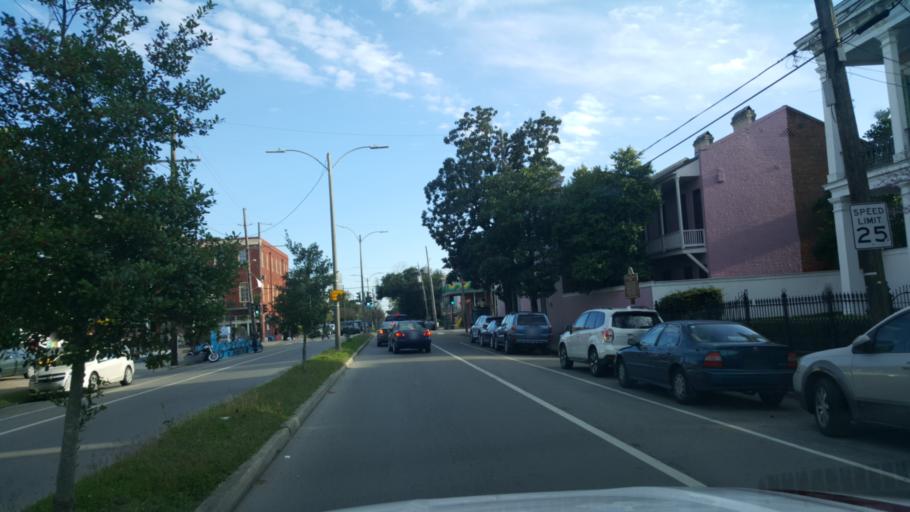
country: US
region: Louisiana
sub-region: Orleans Parish
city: New Orleans
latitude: 29.9303
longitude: -90.0773
